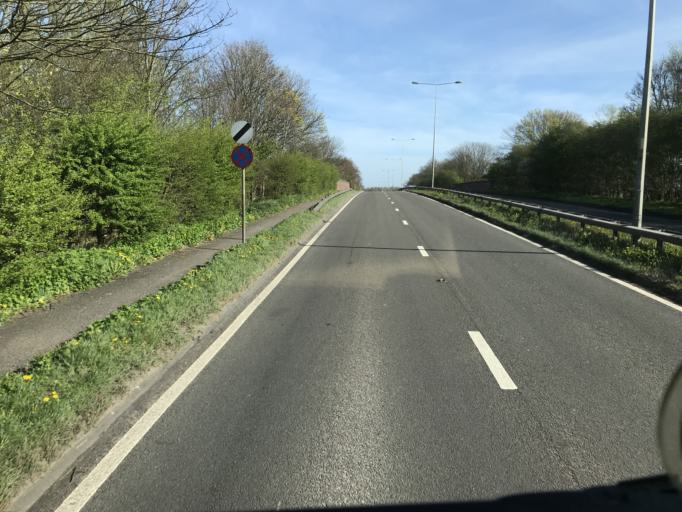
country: GB
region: England
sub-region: Cheshire West and Chester
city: Marston
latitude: 53.2673
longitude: -2.4564
